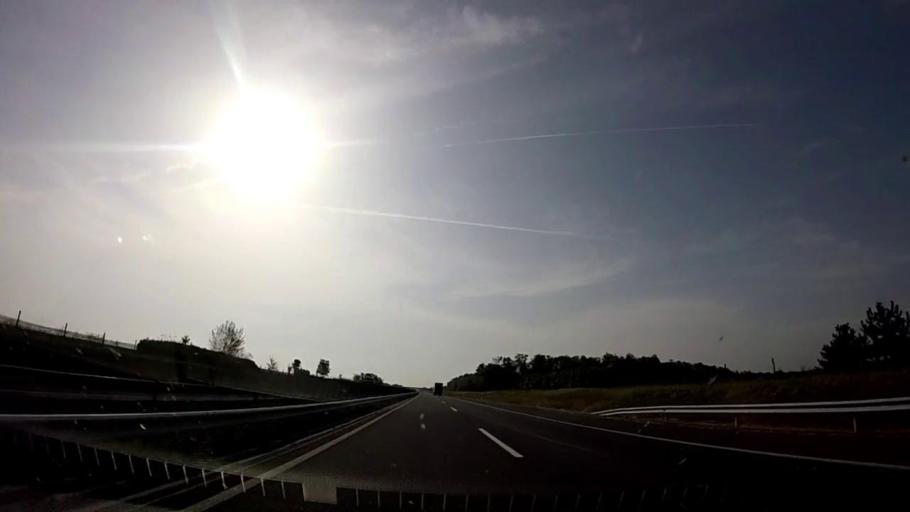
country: HU
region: Zala
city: Zalakomar
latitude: 46.5951
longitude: 17.2509
